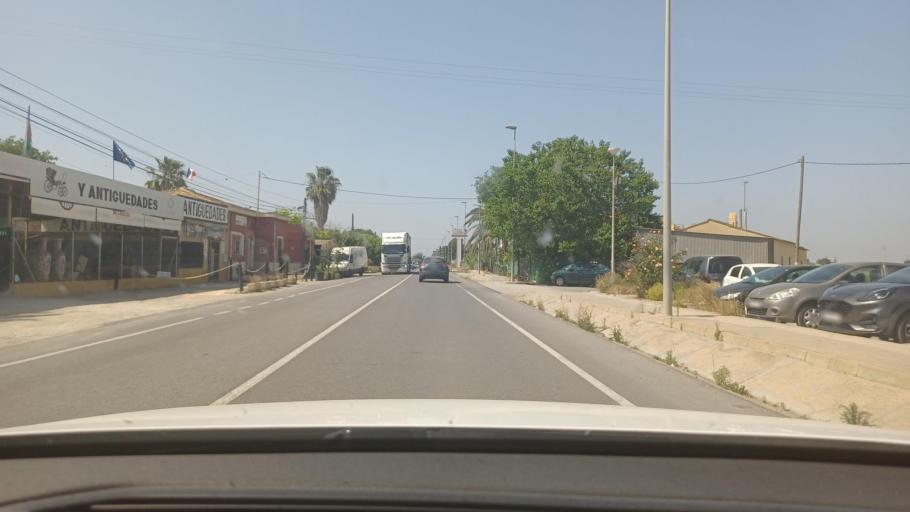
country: ES
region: Valencia
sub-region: Provincia de Alicante
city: Dolores
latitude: 38.1341
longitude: -0.7735
